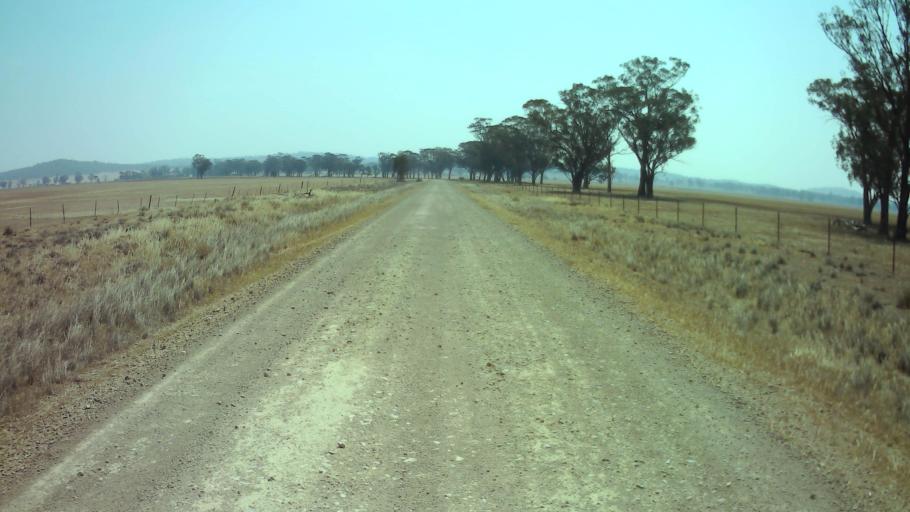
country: AU
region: New South Wales
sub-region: Weddin
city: Grenfell
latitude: -33.6374
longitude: 148.2450
